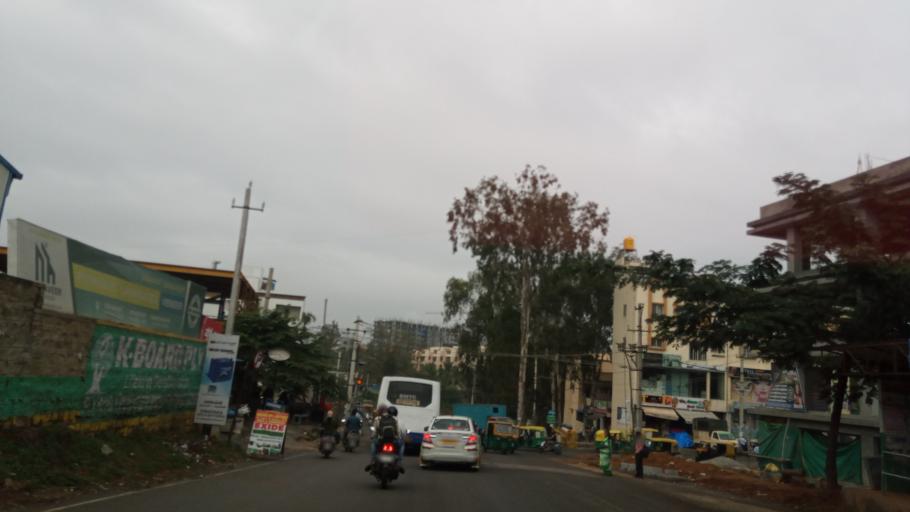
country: IN
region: Karnataka
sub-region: Bangalore Urban
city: Bangalore
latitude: 12.9040
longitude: 77.5129
